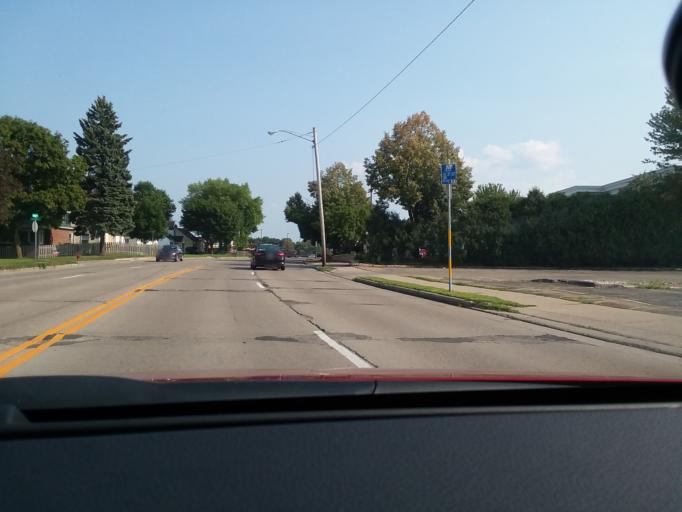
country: US
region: Wisconsin
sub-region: Dane County
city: Monona
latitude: 43.0865
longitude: -89.3263
